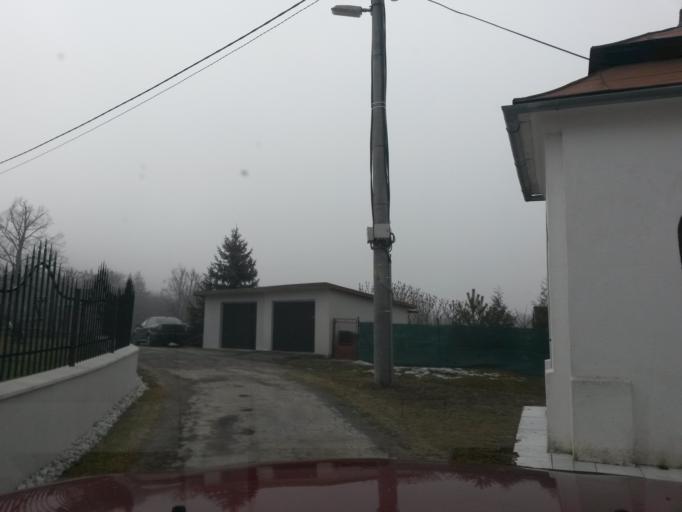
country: SK
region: Kosicky
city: Gelnica
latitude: 48.8772
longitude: 20.9948
